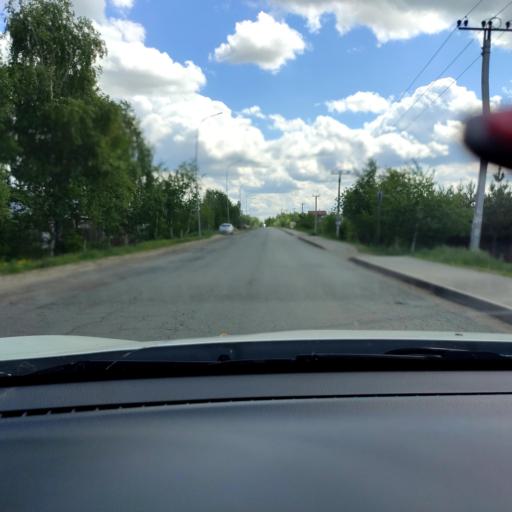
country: RU
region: Tatarstan
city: Stolbishchi
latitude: 55.6970
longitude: 49.1917
